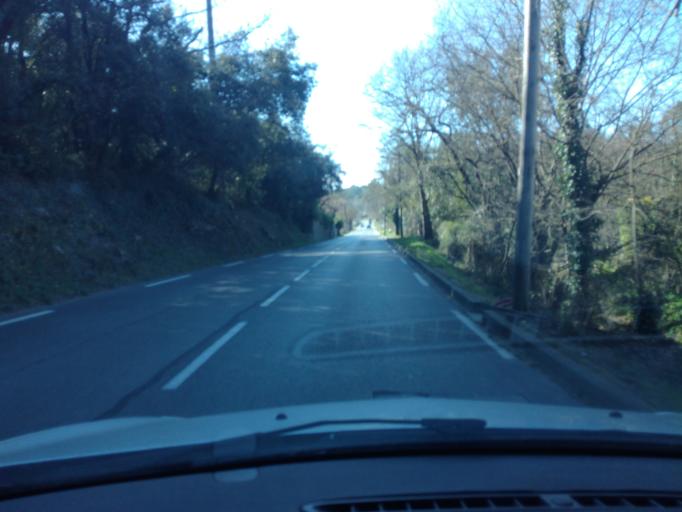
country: FR
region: Provence-Alpes-Cote d'Azur
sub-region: Departement des Alpes-Maritimes
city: Pegomas
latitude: 43.6313
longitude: 6.9313
